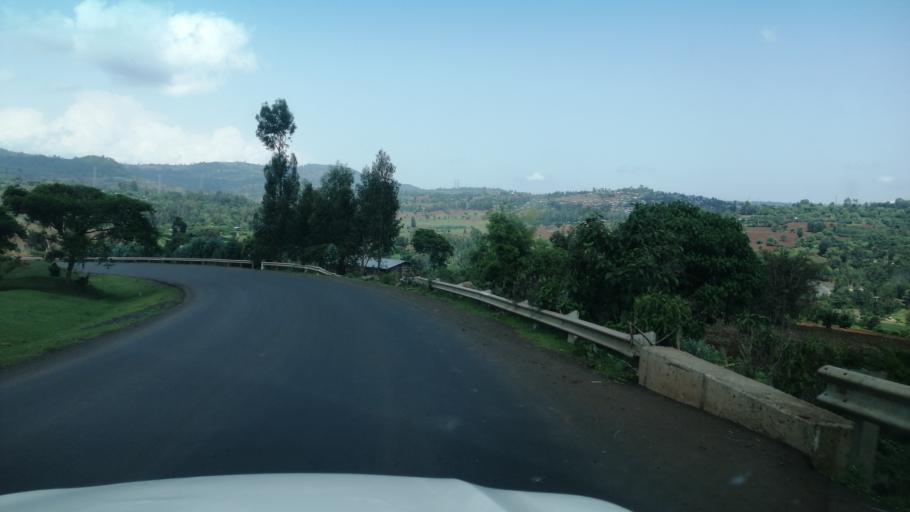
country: ET
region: Oromiya
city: Gedo
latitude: 8.9770
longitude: 37.5591
